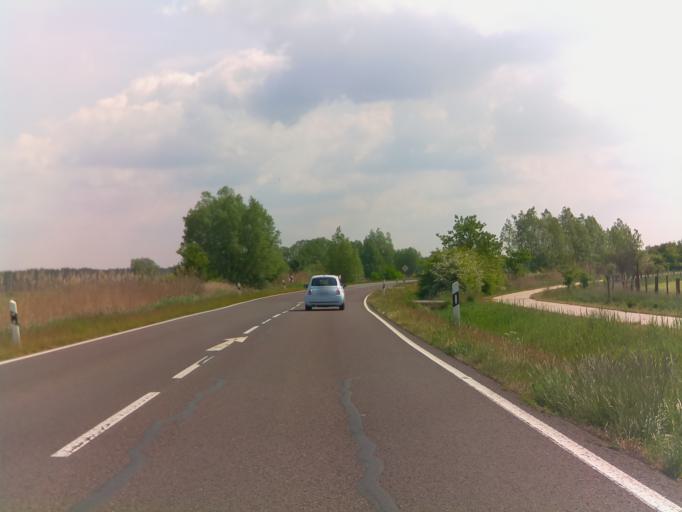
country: DE
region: Saxony-Anhalt
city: Schonhausen
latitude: 52.5509
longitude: 12.0737
